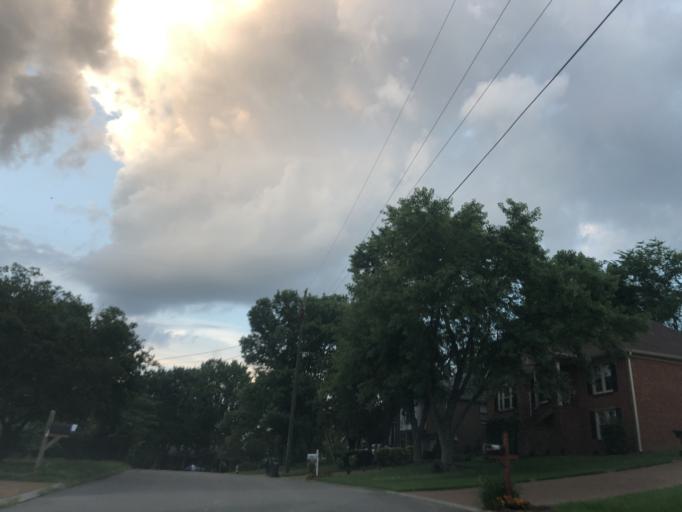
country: US
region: Tennessee
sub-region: Davidson County
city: Lakewood
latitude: 36.1470
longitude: -86.6333
